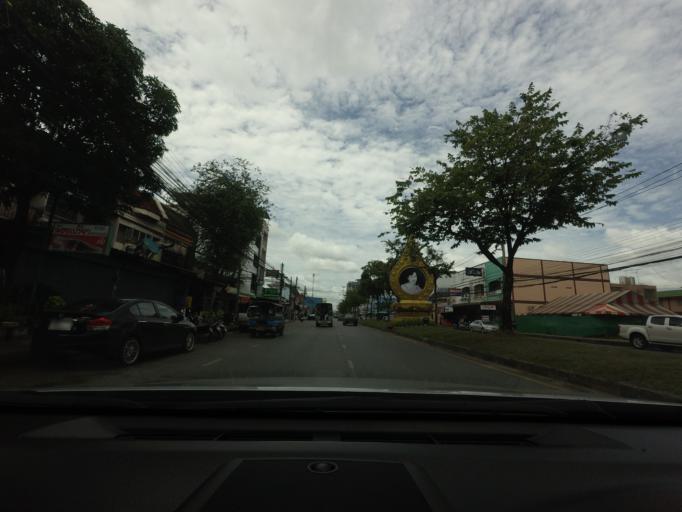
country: TH
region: Songkhla
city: Hat Yai
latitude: 7.0094
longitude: 100.4590
